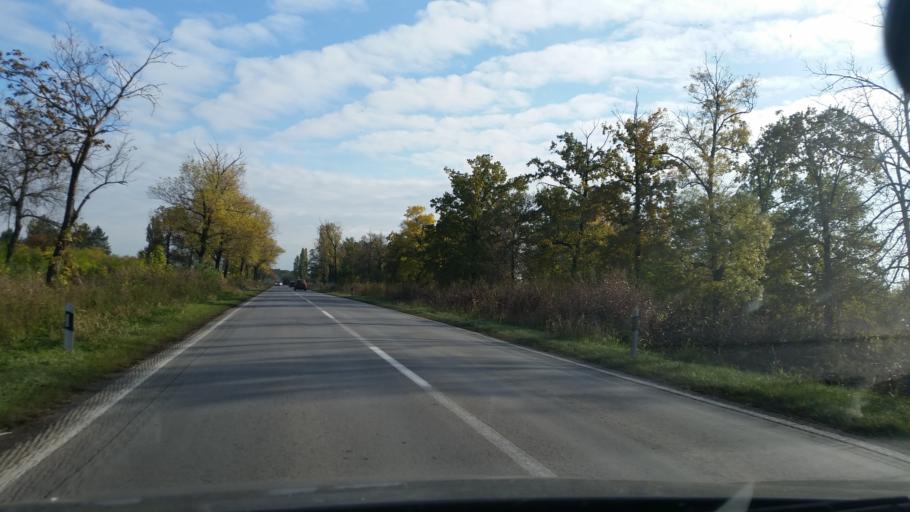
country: RS
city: Ecka
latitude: 45.3384
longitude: 20.4330
